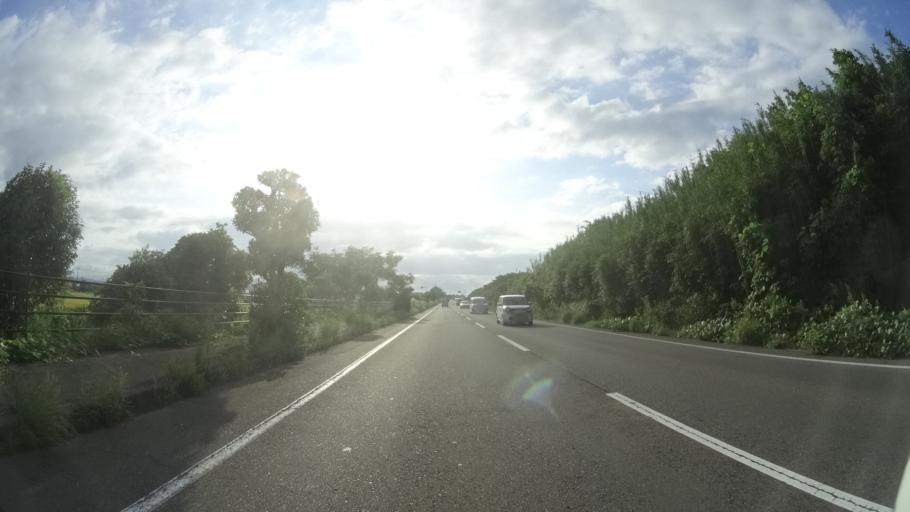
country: JP
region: Tottori
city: Kurayoshi
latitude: 35.4951
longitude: 133.8509
